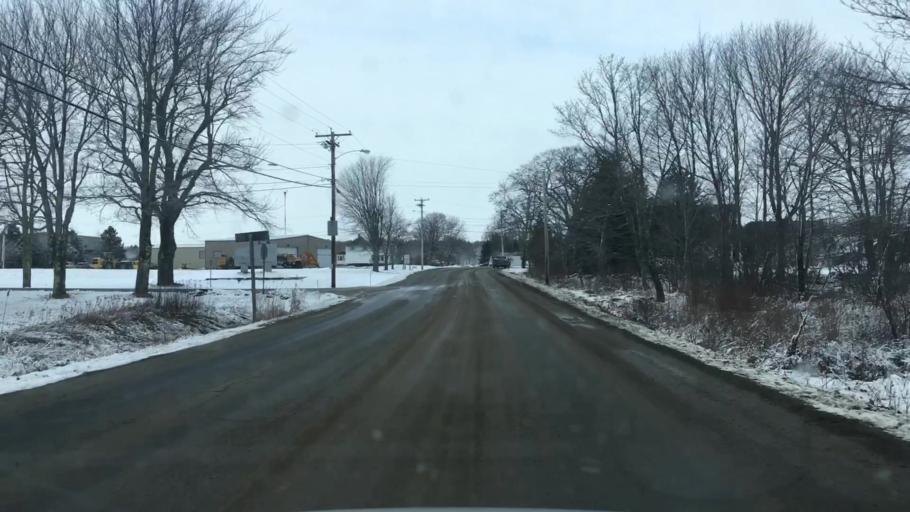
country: US
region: Maine
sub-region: Knox County
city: South Thomaston
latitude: 44.0615
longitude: -69.0918
